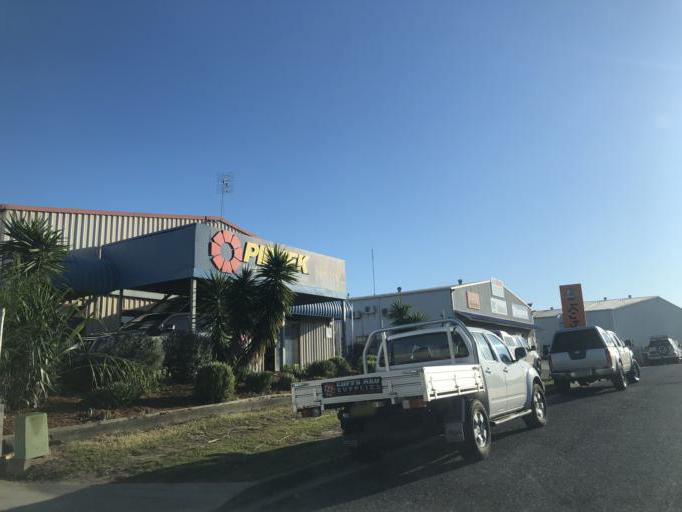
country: AU
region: New South Wales
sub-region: Coffs Harbour
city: Coffs Harbour
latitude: -30.3102
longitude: 153.0997
